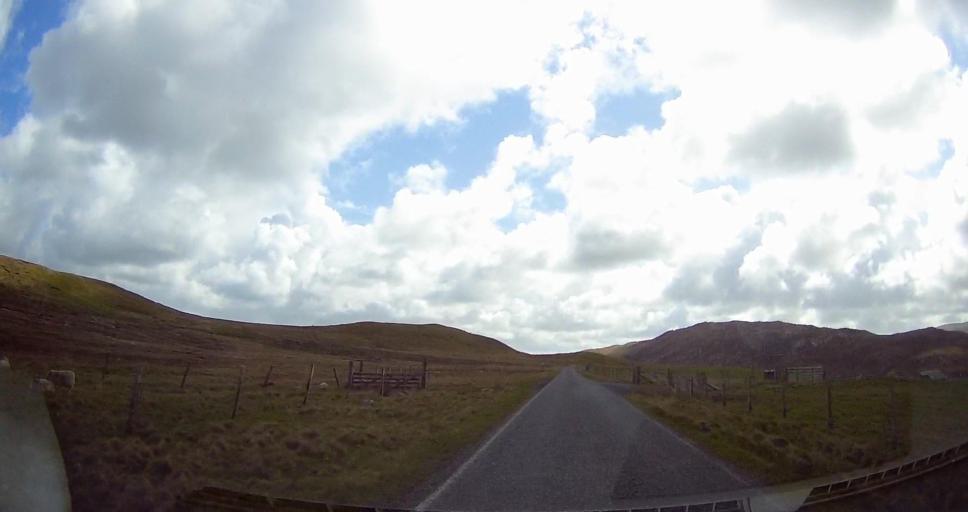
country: GB
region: Scotland
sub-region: Shetland Islands
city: Lerwick
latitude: 60.5608
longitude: -1.3340
